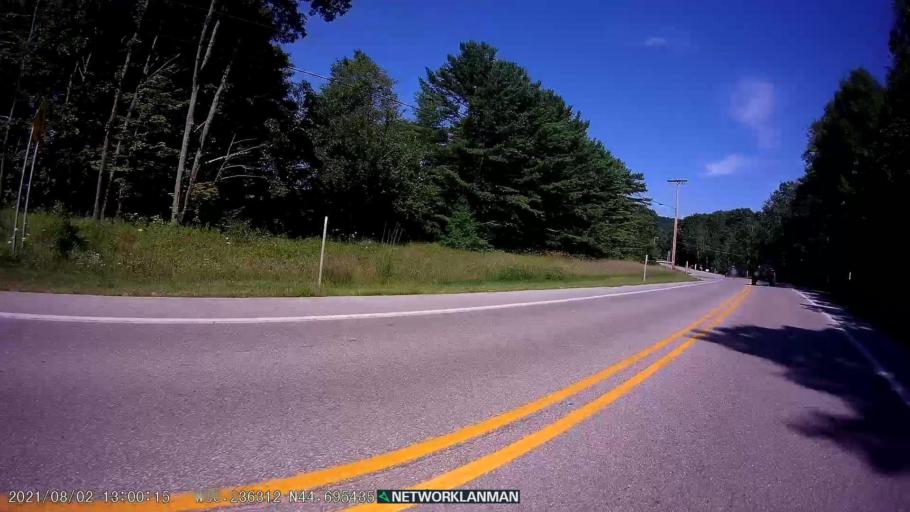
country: US
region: Michigan
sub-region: Benzie County
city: Frankfort
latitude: 44.6955
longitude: -86.2358
